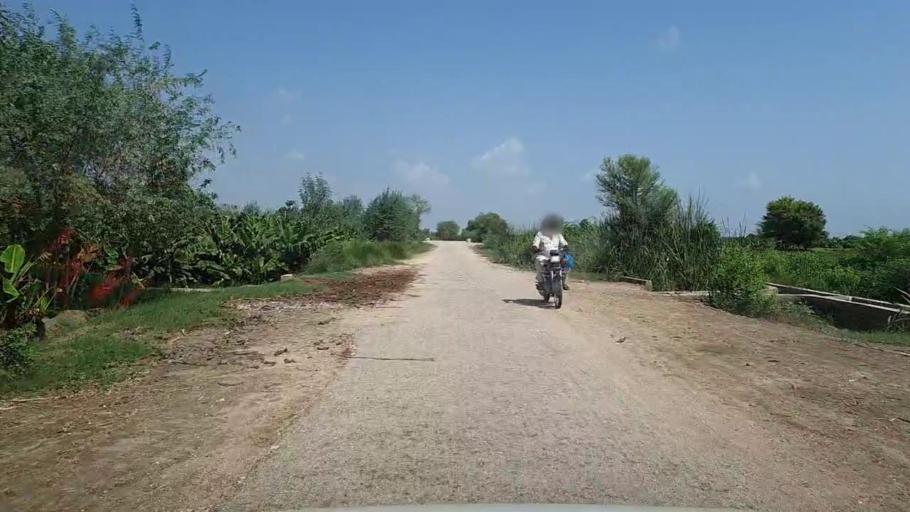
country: PK
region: Sindh
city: Bhiria
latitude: 26.8694
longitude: 68.2569
